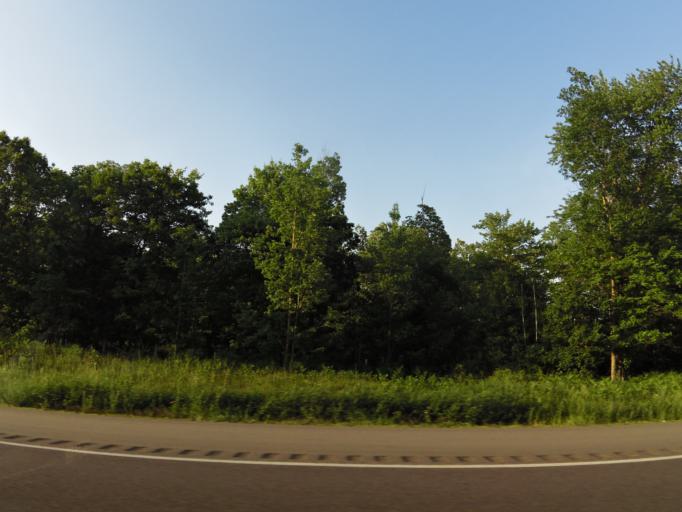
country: US
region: Wisconsin
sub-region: Jackson County
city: Black River Falls
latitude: 44.2189
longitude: -90.6873
